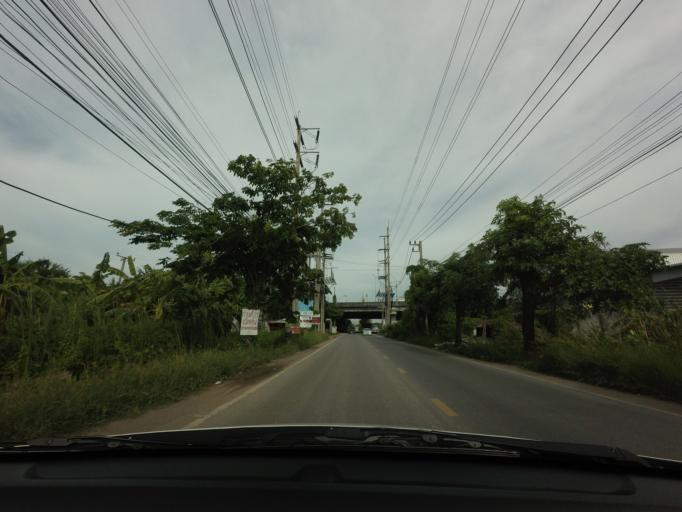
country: TH
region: Bangkok
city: Bang Na
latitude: 13.6184
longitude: 100.6613
